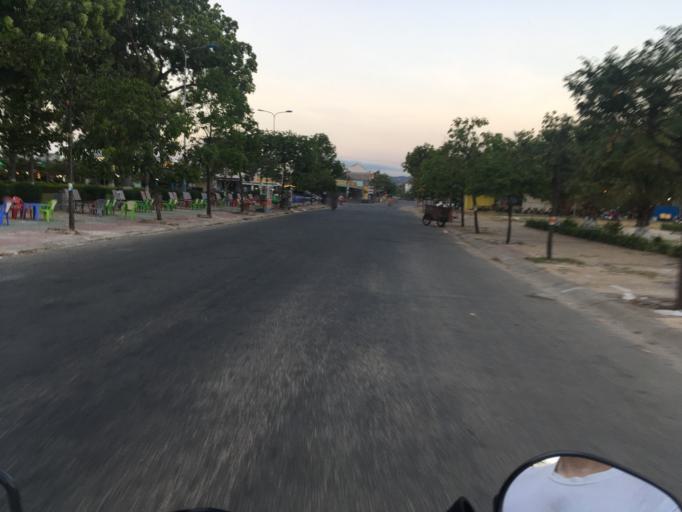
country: VN
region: Ninh Thuan
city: Phan Rang-Thap Cham
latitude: 11.5665
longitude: 108.9984
